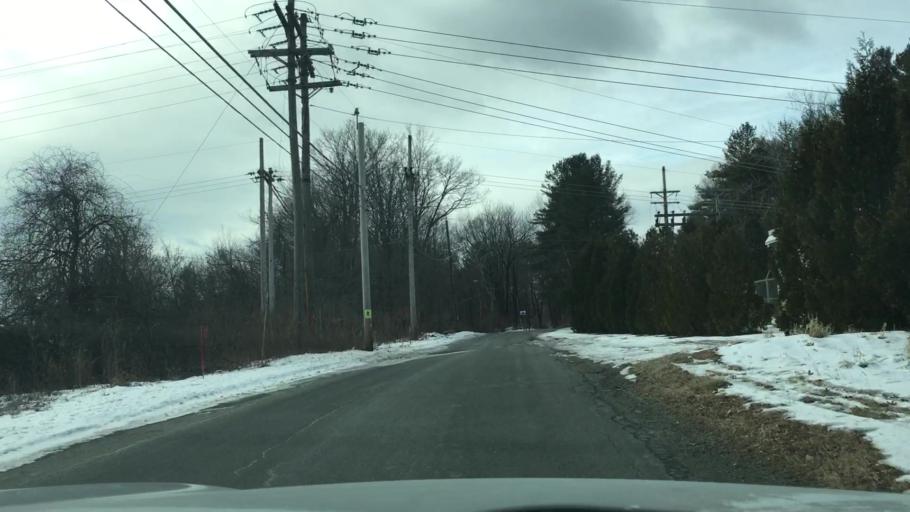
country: US
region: Massachusetts
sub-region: Berkshire County
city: Lee
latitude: 42.3359
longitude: -73.2345
